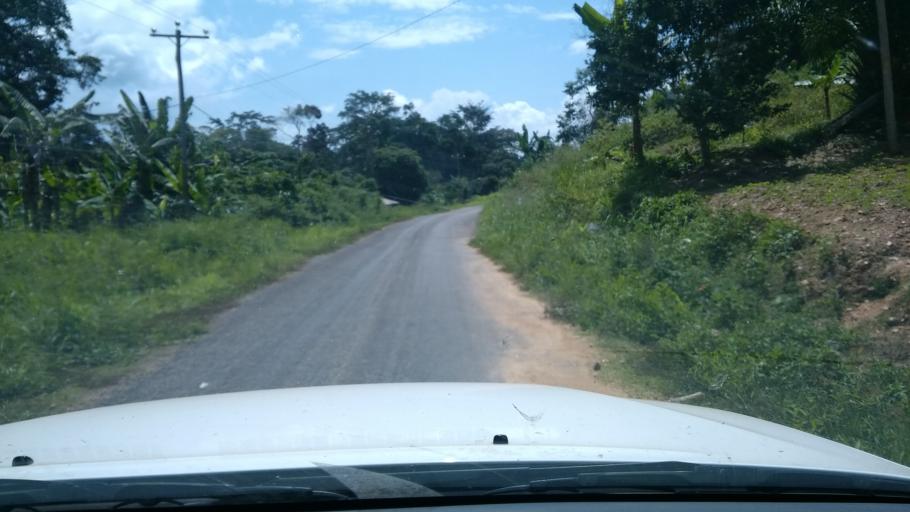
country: CM
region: Centre
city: Evodoula
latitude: 4.1460
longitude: 11.2779
